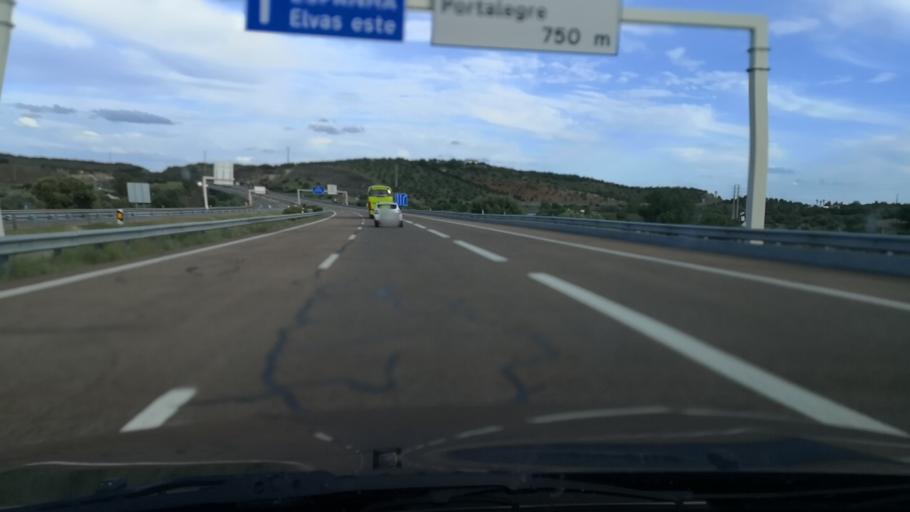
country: PT
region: Portalegre
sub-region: Elvas
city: Elvas
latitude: 38.9052
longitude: -7.1573
